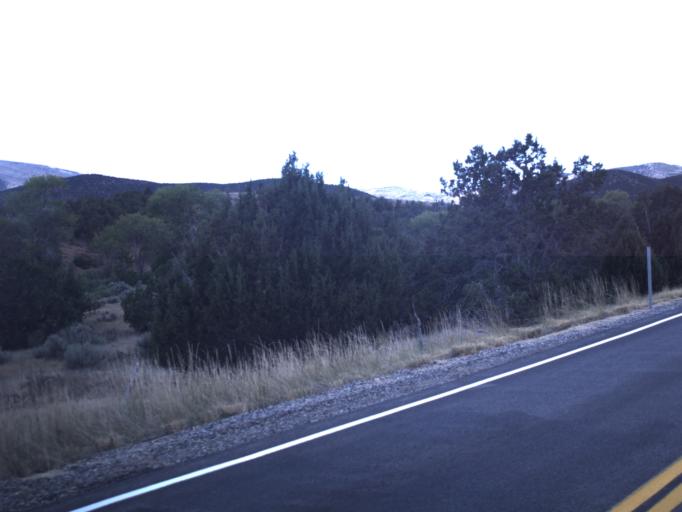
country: US
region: Utah
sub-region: Tooele County
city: Grantsville
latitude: 40.3325
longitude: -112.5171
